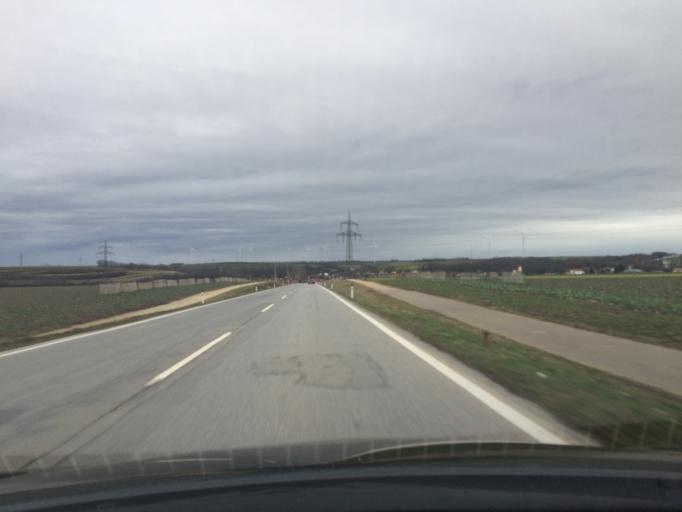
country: AT
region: Lower Austria
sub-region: Politischer Bezirk Mistelbach
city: Wilfersdorf
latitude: 48.5732
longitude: 16.6865
